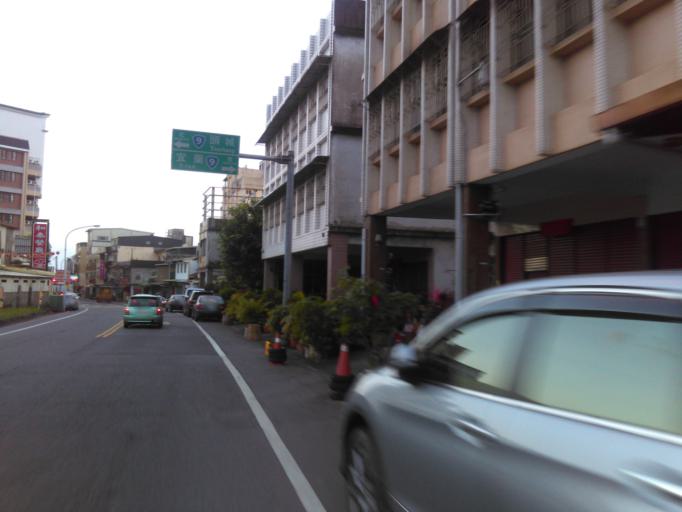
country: TW
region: Taiwan
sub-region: Yilan
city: Yilan
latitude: 24.8199
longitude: 121.7672
